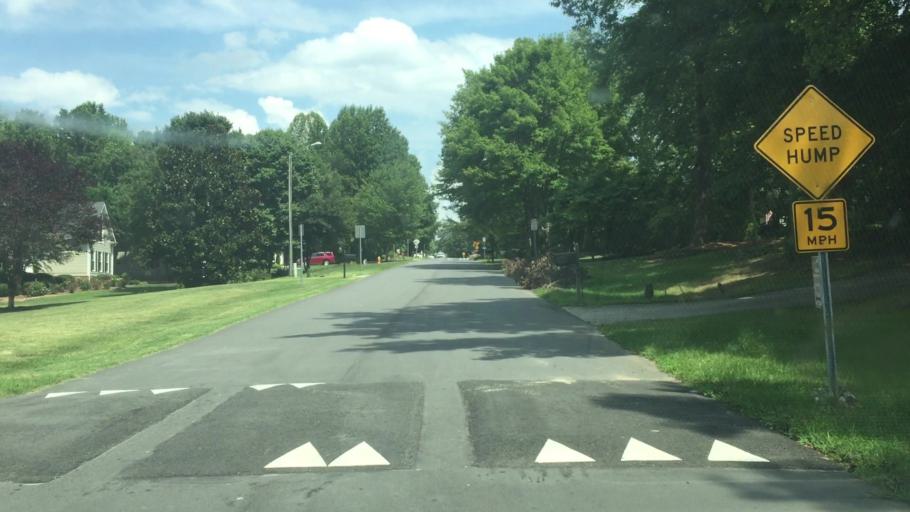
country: US
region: North Carolina
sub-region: Iredell County
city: Mooresville
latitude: 35.5518
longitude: -80.7952
